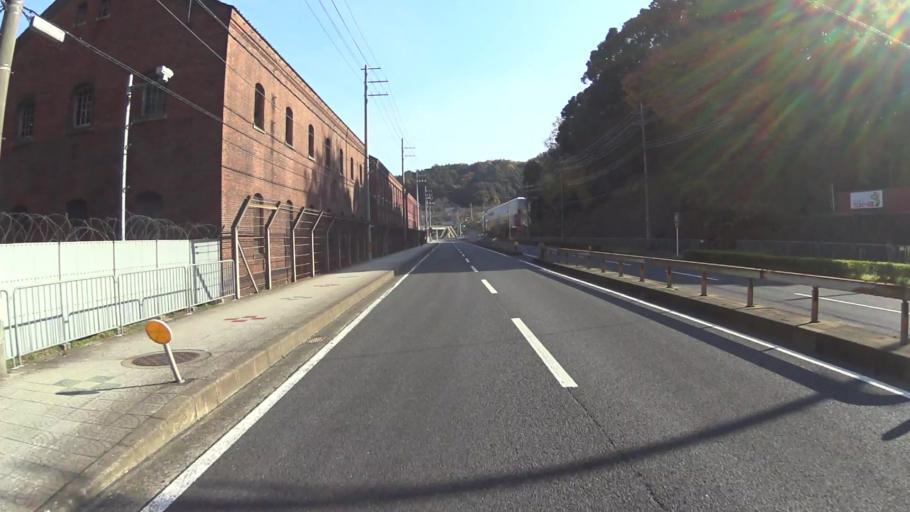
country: JP
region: Kyoto
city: Maizuru
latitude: 35.4760
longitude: 135.3789
